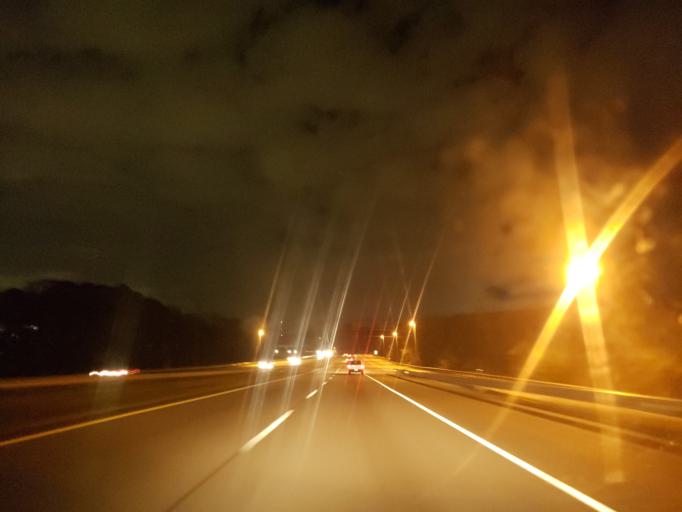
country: US
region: Georgia
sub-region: Chatham County
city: Thunderbolt
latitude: 32.0251
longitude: -81.0883
